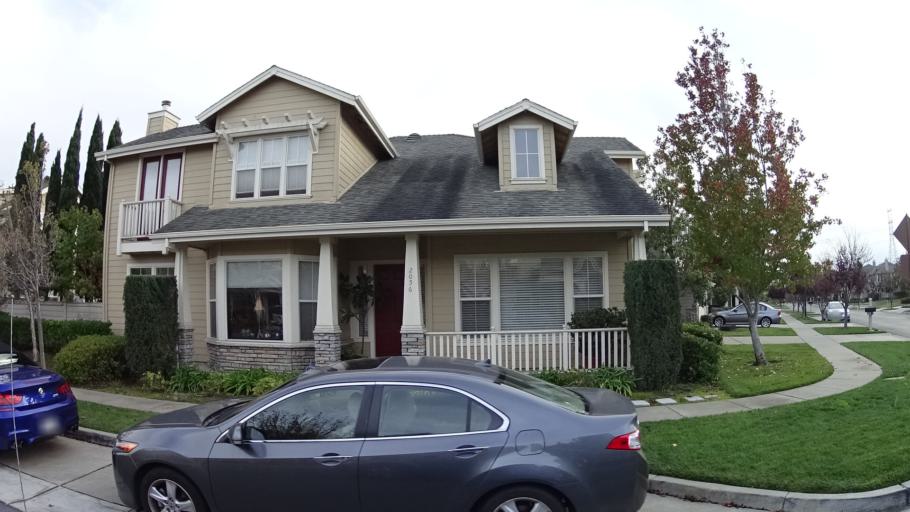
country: US
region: California
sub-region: San Mateo County
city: Redwood Shores
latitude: 37.5472
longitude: -122.2387
